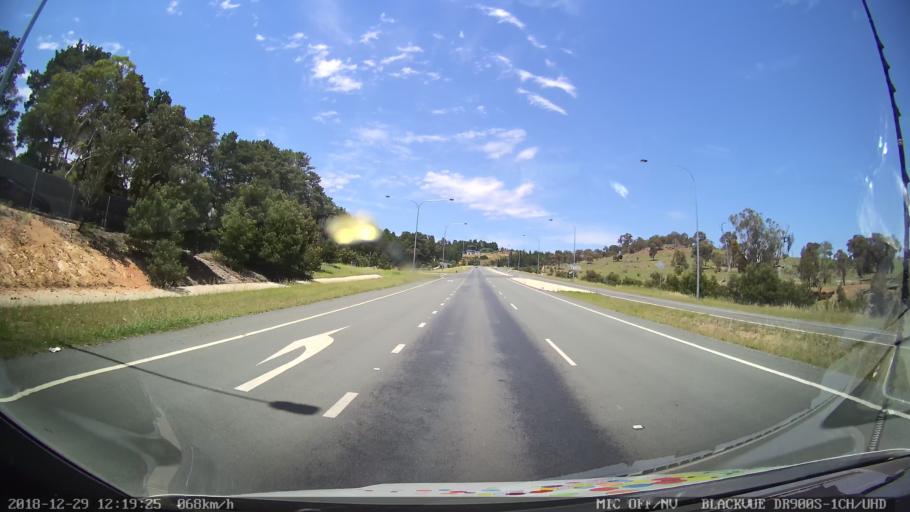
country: AU
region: New South Wales
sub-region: Queanbeyan
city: Queanbeyan
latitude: -35.3936
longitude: 149.2333
